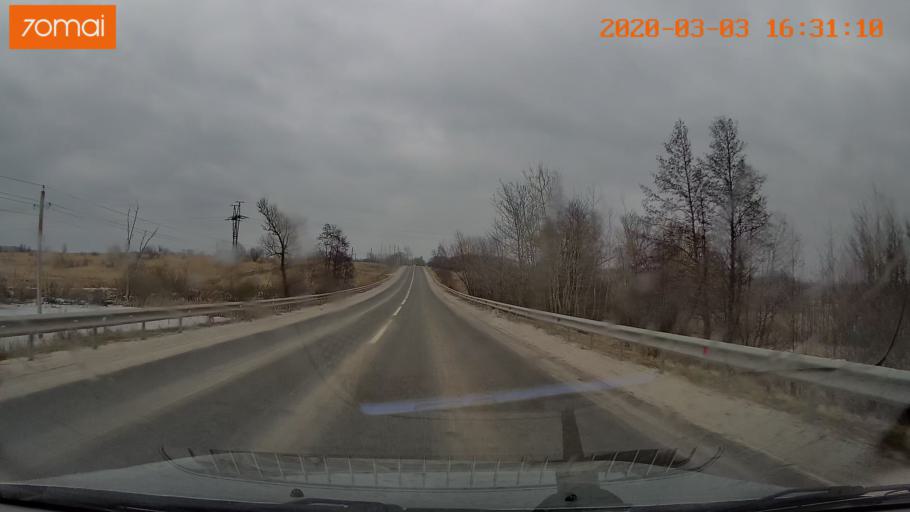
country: RU
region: Moskovskaya
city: Konobeyevo
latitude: 55.4274
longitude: 38.7210
